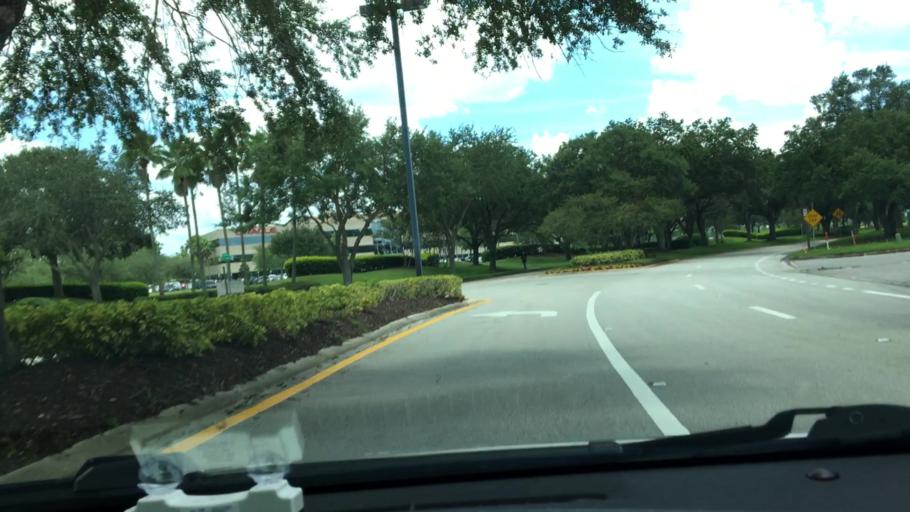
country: US
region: Florida
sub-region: Orange County
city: Conway
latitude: 28.4590
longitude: -81.3048
